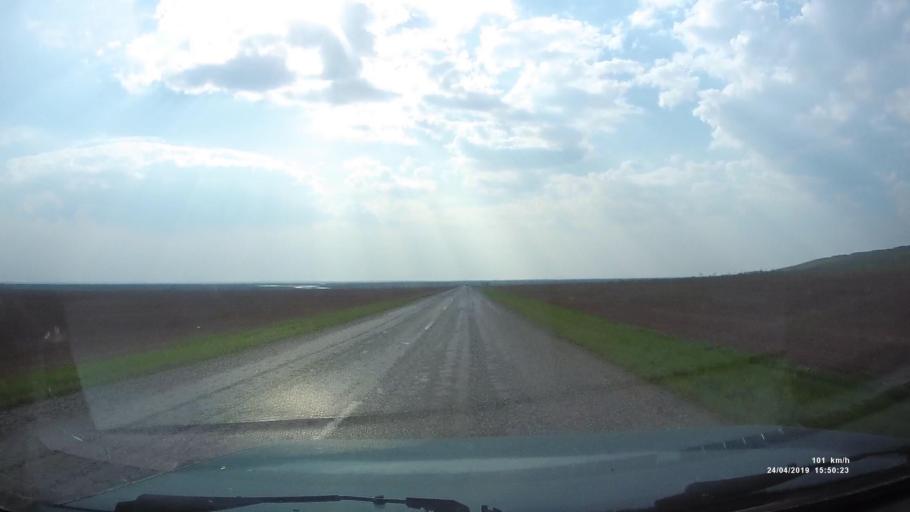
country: RU
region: Kalmykiya
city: Yashalta
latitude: 46.6041
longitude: 42.6340
